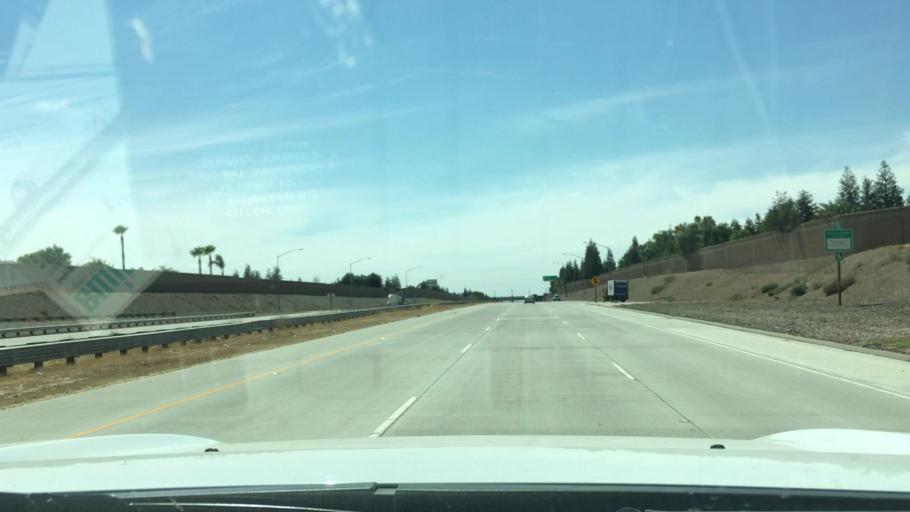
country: US
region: California
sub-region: Kern County
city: Greenacres
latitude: 35.3621
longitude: -119.1183
